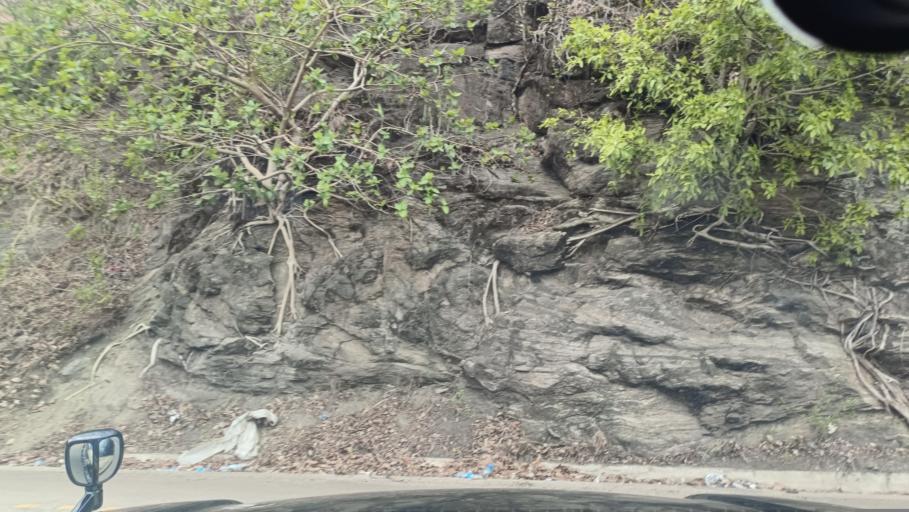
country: TZ
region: Morogoro
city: Kidatu
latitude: -7.5732
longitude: 36.7397
